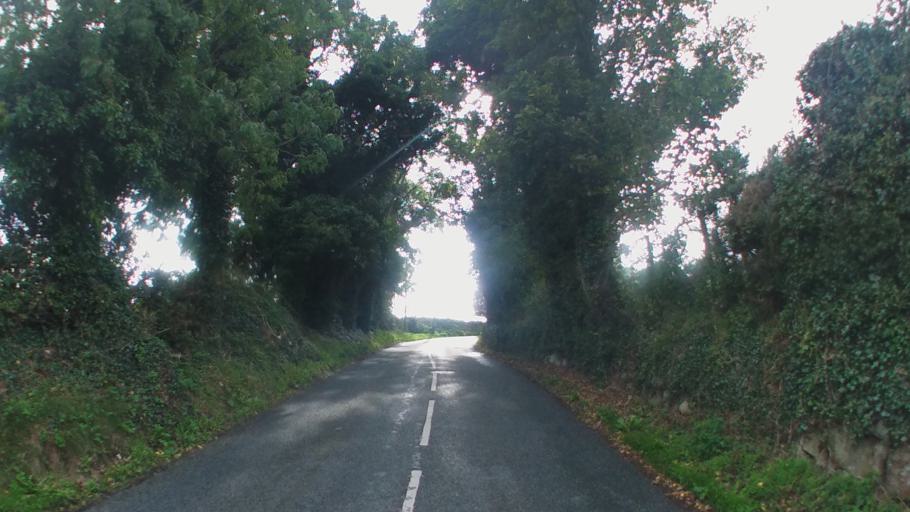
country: IE
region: Leinster
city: Sandyford
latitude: 53.2496
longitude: -6.2147
